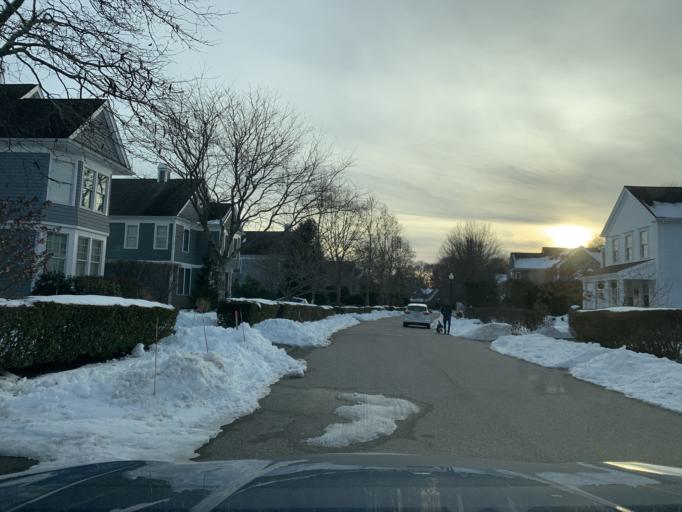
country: US
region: Rhode Island
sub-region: Washington County
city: North Kingstown
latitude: 41.5861
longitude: -71.4466
